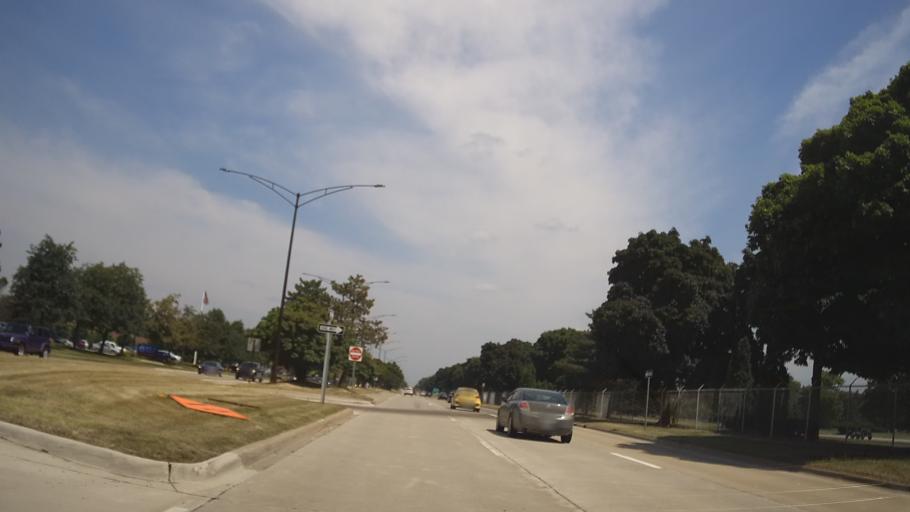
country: US
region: Michigan
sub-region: Oakland County
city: Troy
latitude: 42.5865
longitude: -83.1685
